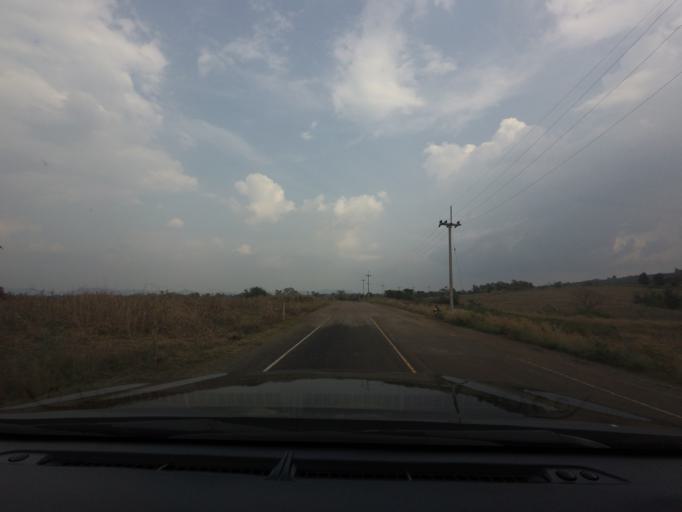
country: TH
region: Nakhon Ratchasima
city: Wang Nam Khiao
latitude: 14.4156
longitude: 101.7642
